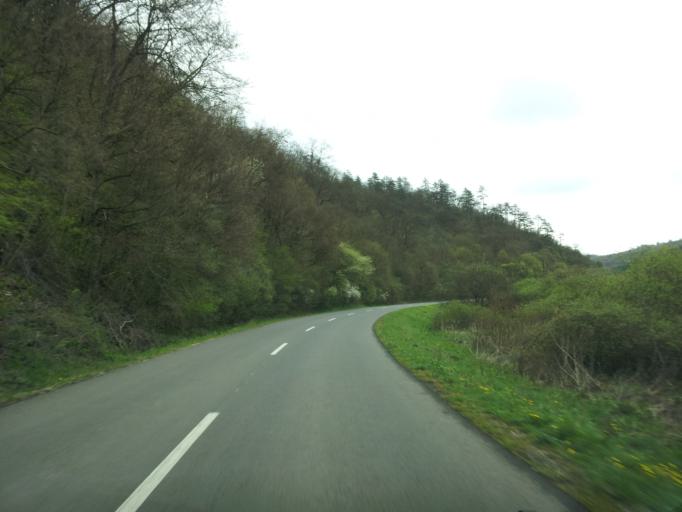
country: HU
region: Borsod-Abauj-Zemplen
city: Rudabanya
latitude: 48.4787
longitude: 20.5814
